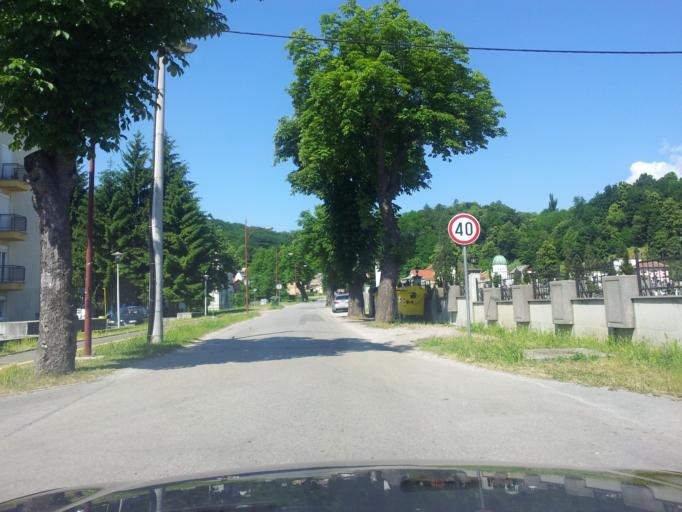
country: HR
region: Karlovacka
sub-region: Grad Karlovac
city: Karlovac
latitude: 45.4929
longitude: 15.5334
